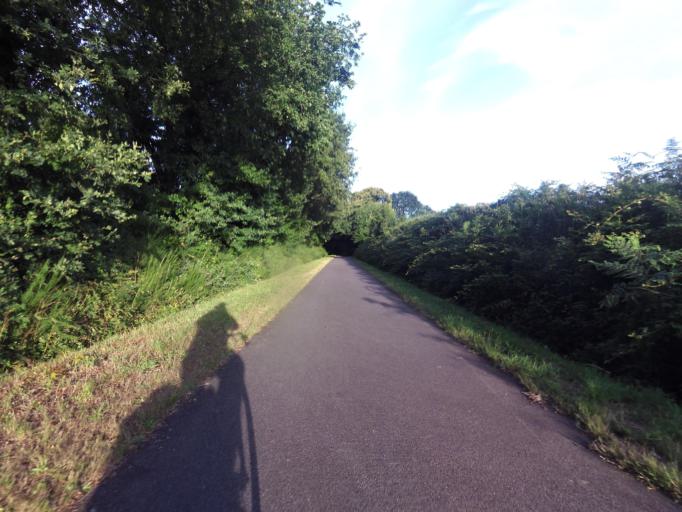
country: FR
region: Brittany
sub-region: Departement du Morbihan
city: Malestroit
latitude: 47.8158
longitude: -2.4118
